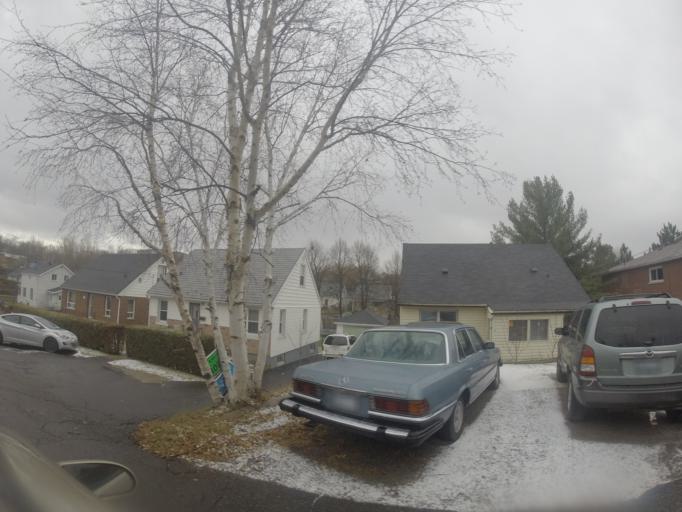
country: CA
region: Ontario
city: Greater Sudbury
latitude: 46.4964
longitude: -81.0106
